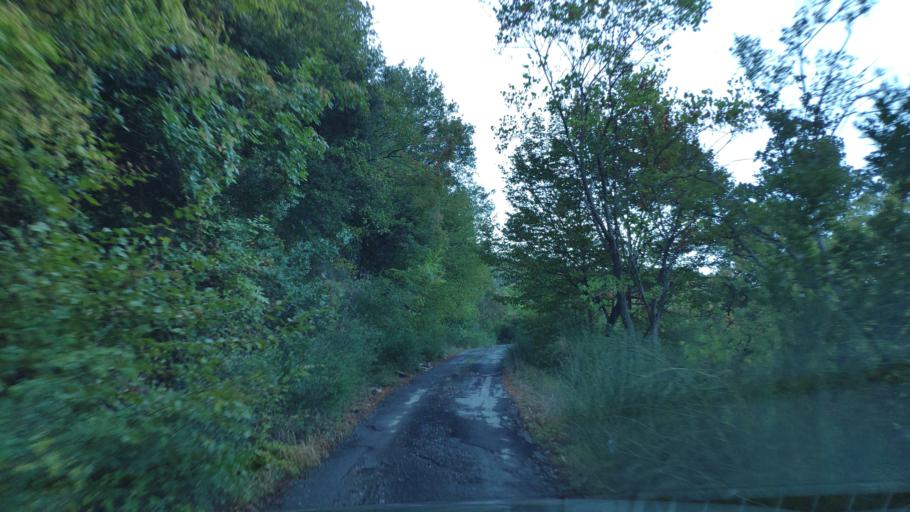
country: GR
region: Peloponnese
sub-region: Nomos Arkadias
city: Dimitsana
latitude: 37.5572
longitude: 22.0452
